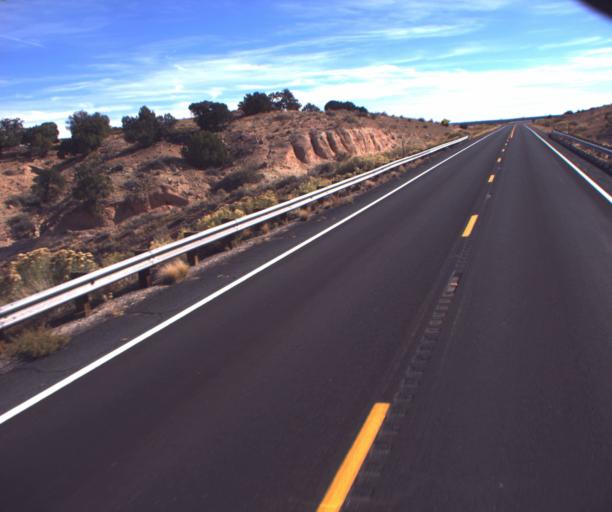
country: US
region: Arizona
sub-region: Coconino County
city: Kaibito
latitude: 36.6147
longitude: -110.9305
